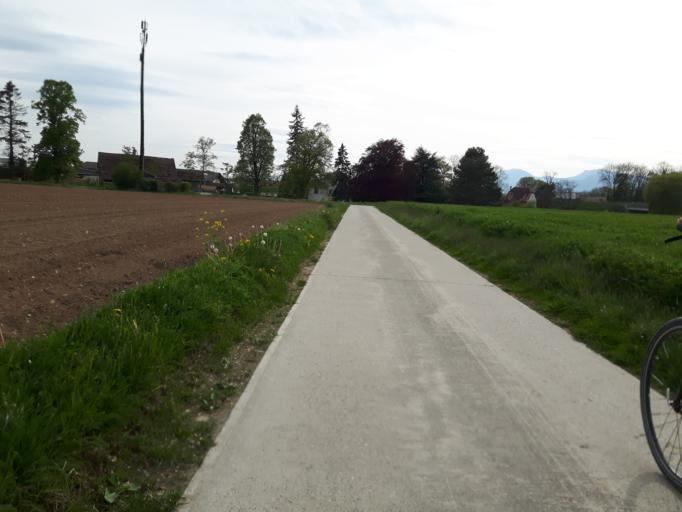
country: CH
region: Vaud
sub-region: Jura-Nord vaudois District
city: Grandson
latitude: 46.8294
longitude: 6.6784
